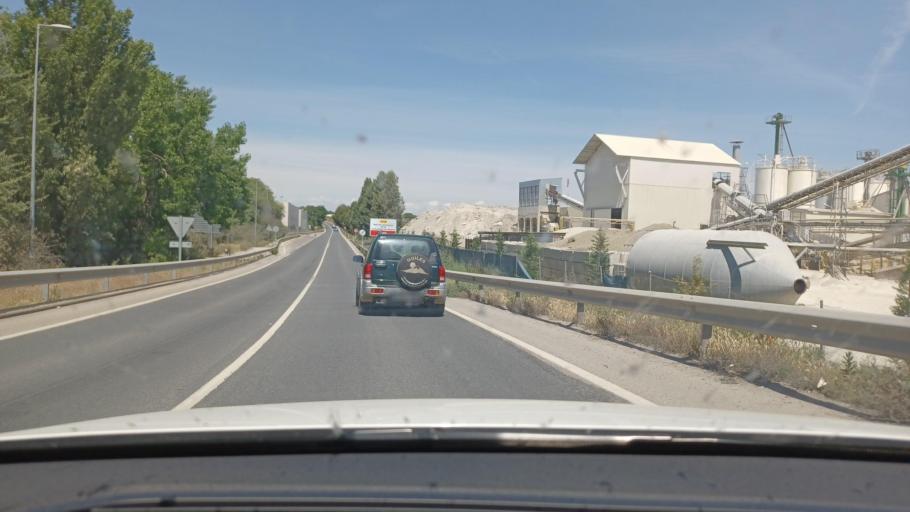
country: ES
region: Madrid
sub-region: Provincia de Madrid
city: Meco
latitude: 40.5329
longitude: -3.2917
